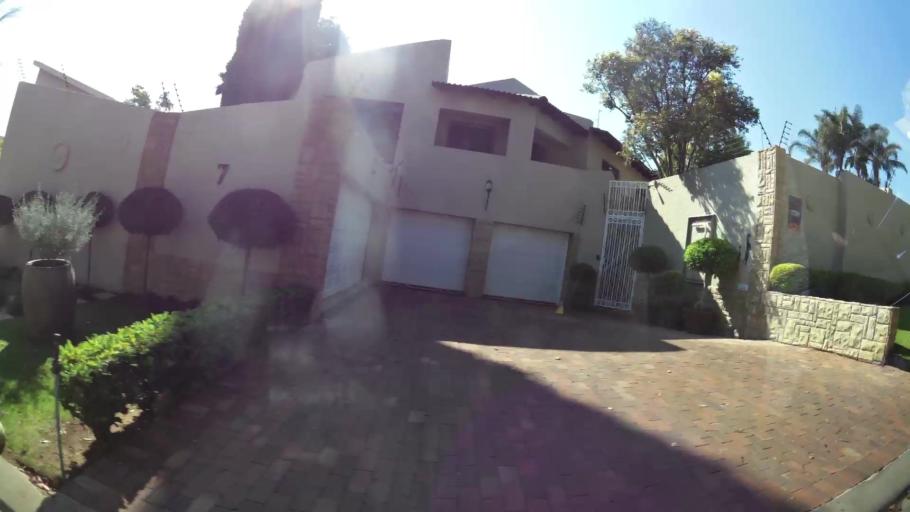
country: ZA
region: Gauteng
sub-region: City of Johannesburg Metropolitan Municipality
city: Johannesburg
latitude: -26.0909
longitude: 28.0478
